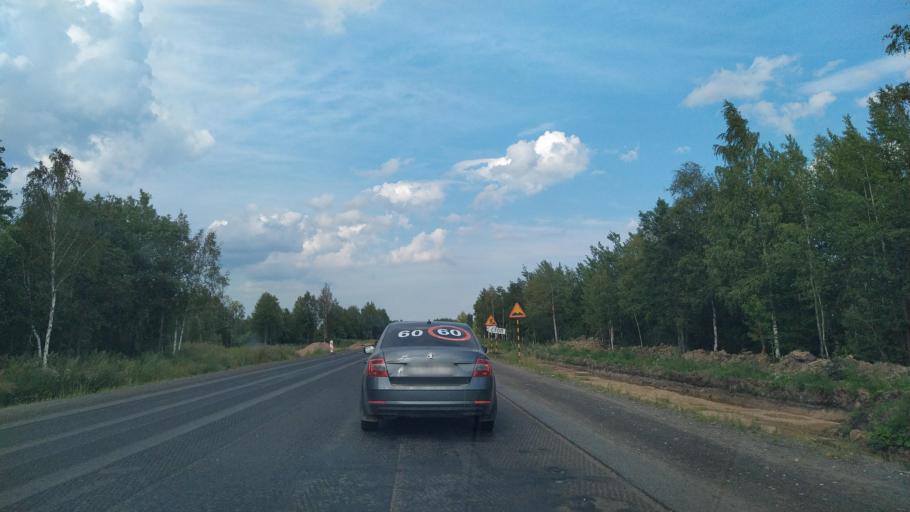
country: RU
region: Novgorod
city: Shimsk
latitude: 58.2916
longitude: 30.8607
